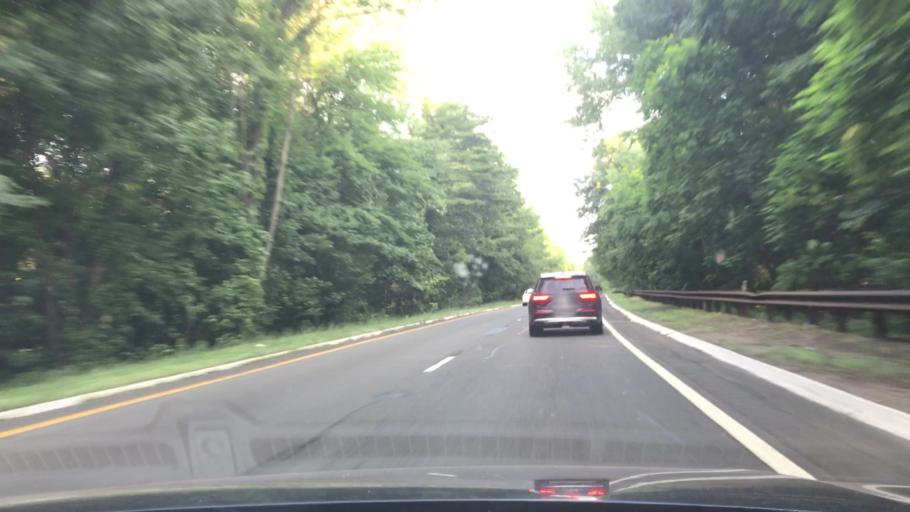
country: US
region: New York
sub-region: Rockland County
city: Bardonia
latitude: 41.1164
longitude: -74.0034
